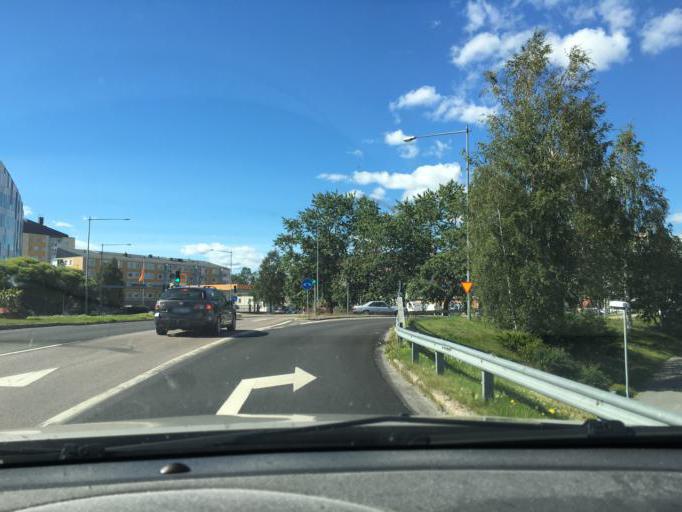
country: SE
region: Norrbotten
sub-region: Lulea Kommun
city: Lulea
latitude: 65.5806
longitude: 22.1462
